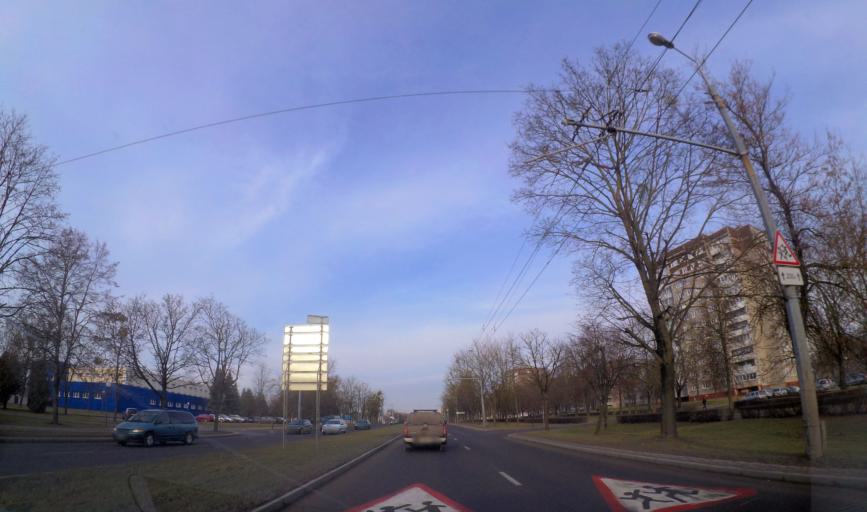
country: BY
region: Grodnenskaya
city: Hrodna
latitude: 53.6907
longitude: 23.8008
